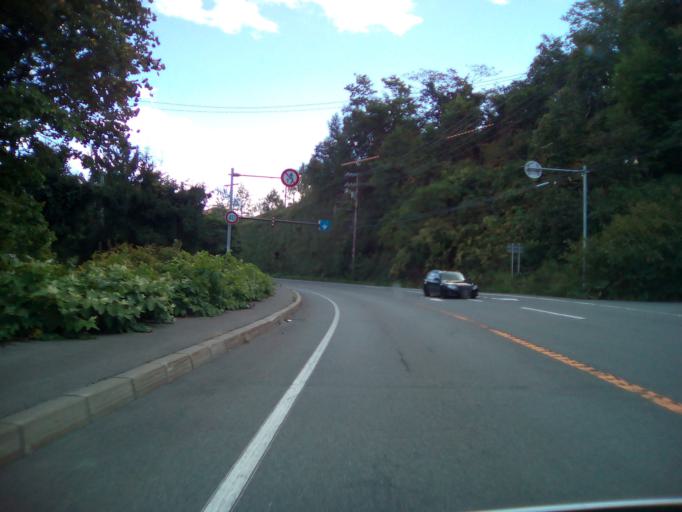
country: JP
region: Hokkaido
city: Date
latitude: 42.5704
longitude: 140.8003
